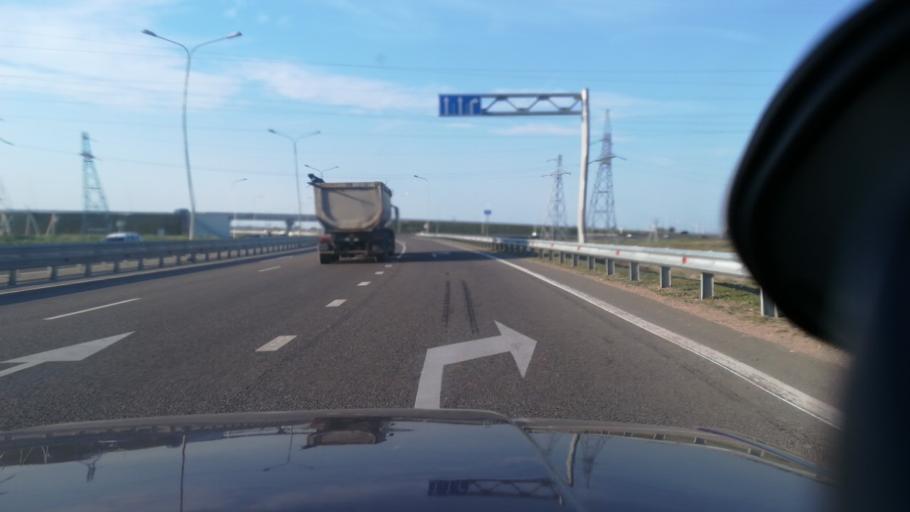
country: RU
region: Krasnodarskiy
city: Dzhiginka
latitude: 45.1342
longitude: 37.3159
